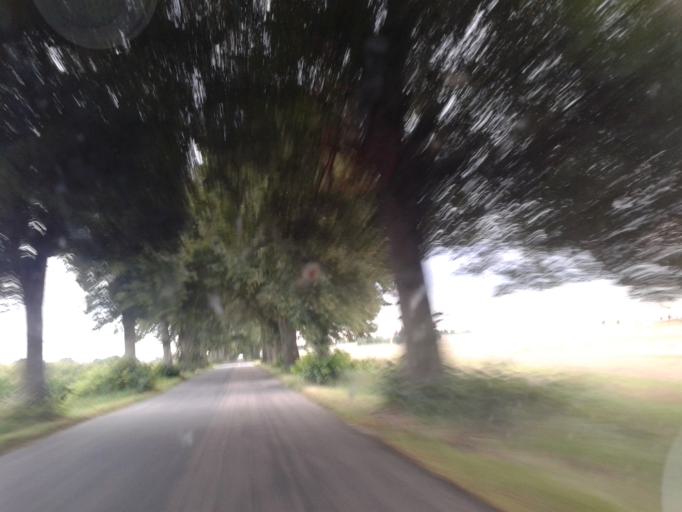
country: PL
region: West Pomeranian Voivodeship
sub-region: Powiat szczecinecki
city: Grzmiaca
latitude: 53.8461
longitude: 16.4519
